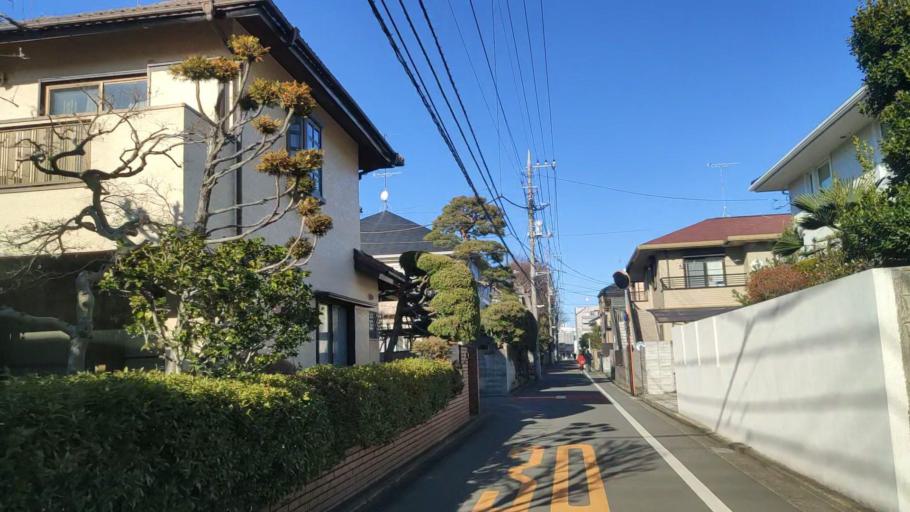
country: JP
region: Tokyo
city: Musashino
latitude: 35.7080
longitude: 139.5716
